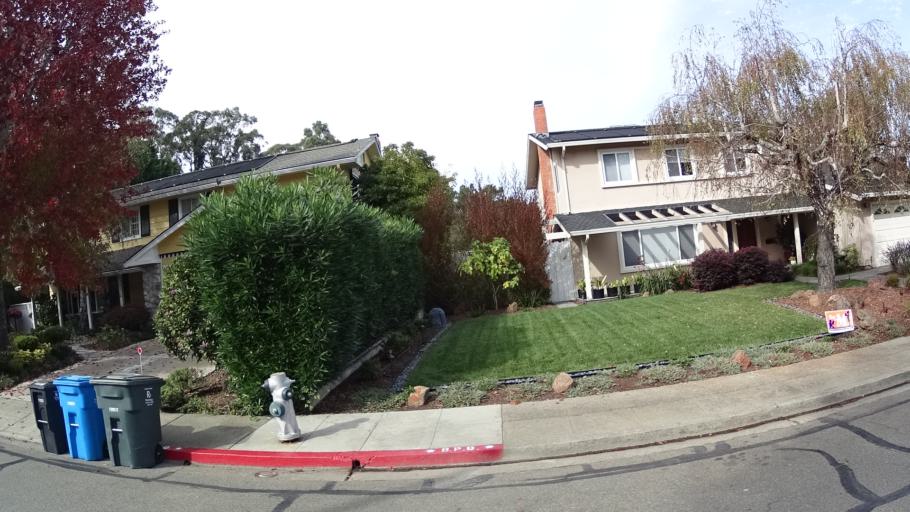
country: US
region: California
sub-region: San Mateo County
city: Hillsborough
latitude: 37.5760
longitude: -122.3974
